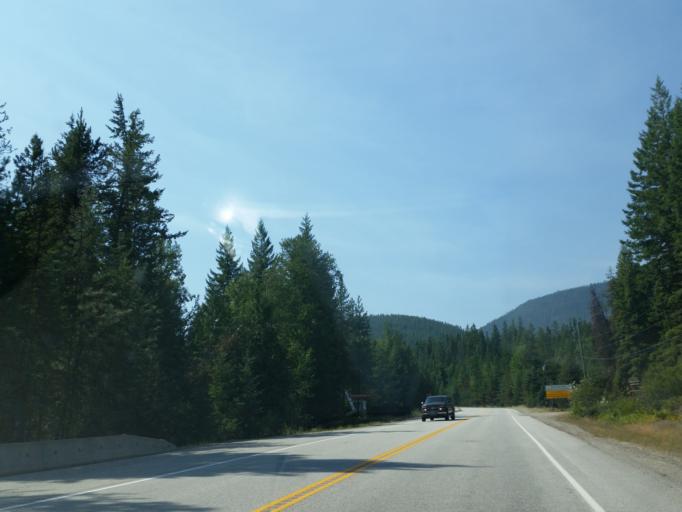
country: CA
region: British Columbia
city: Castlegar
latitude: 49.2777
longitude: -117.6671
